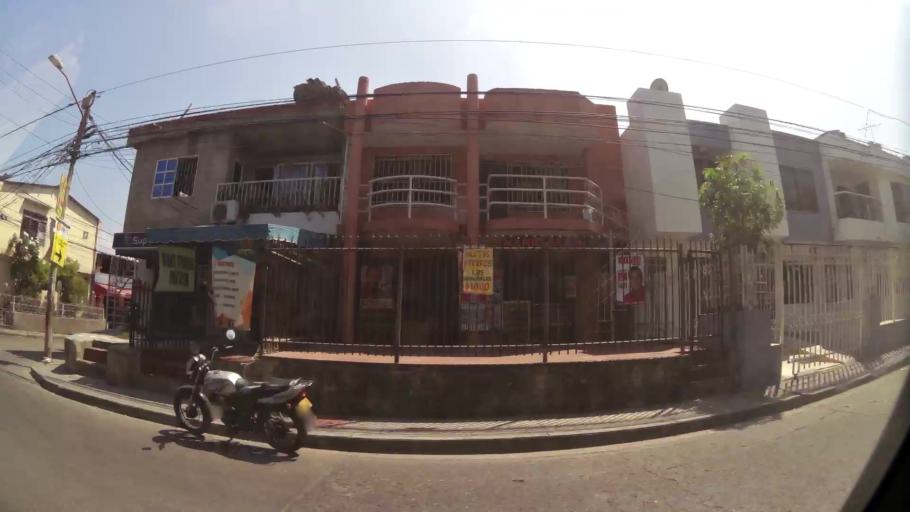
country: CO
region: Bolivar
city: Cartagena
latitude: 10.4013
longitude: -75.4884
